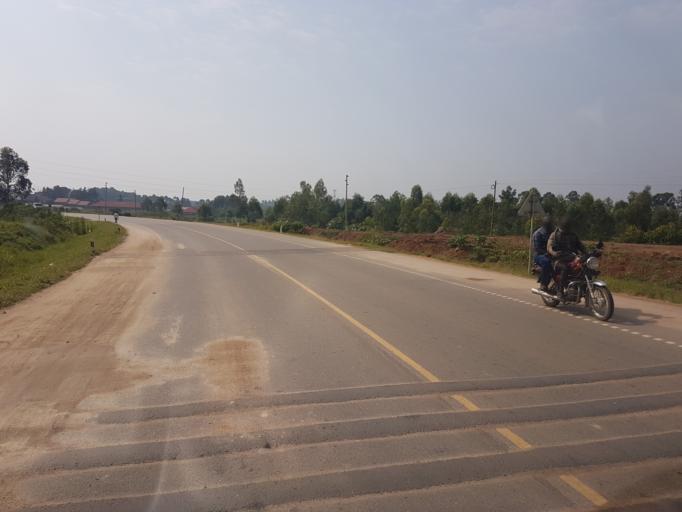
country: UG
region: Western Region
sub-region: Mbarara District
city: Bwizibwera
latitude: -0.6370
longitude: 30.6045
